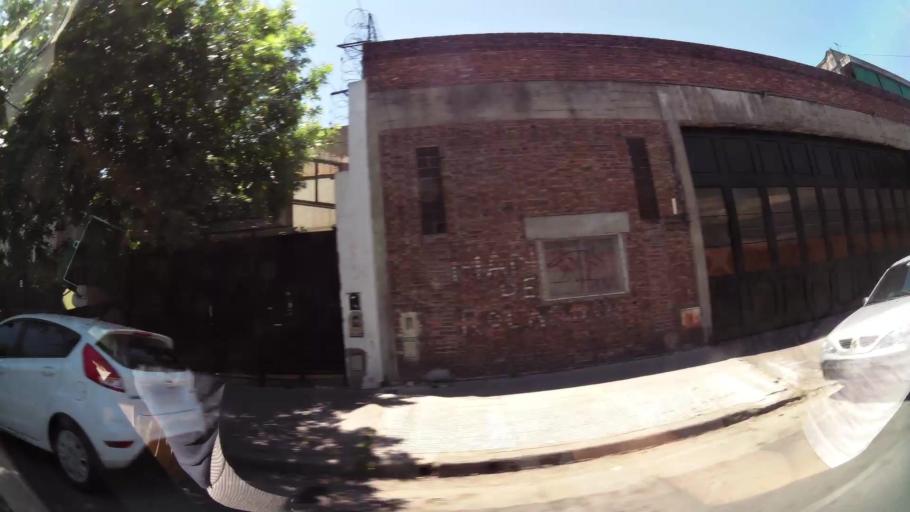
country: AR
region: Buenos Aires
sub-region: Partido de Avellaneda
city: Avellaneda
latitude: -34.6468
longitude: -58.3780
